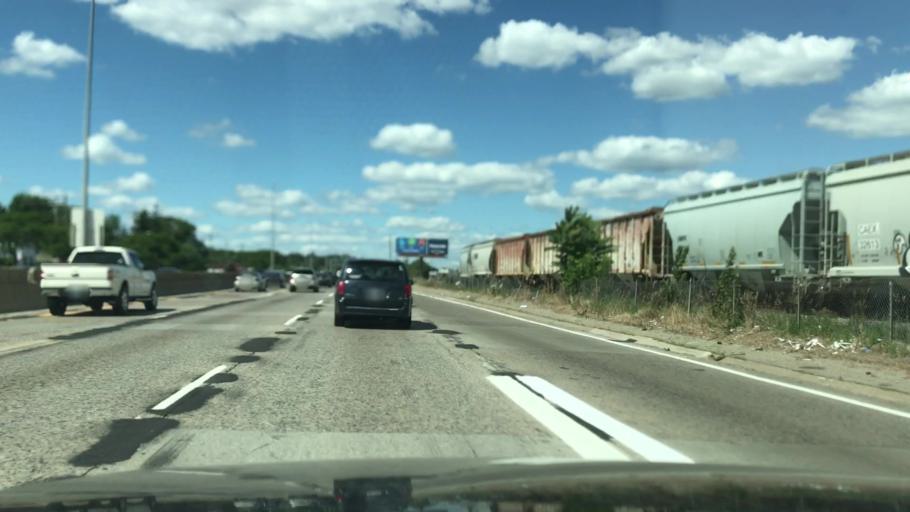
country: US
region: Michigan
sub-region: Kent County
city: Wyoming
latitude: 42.9303
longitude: -85.6812
